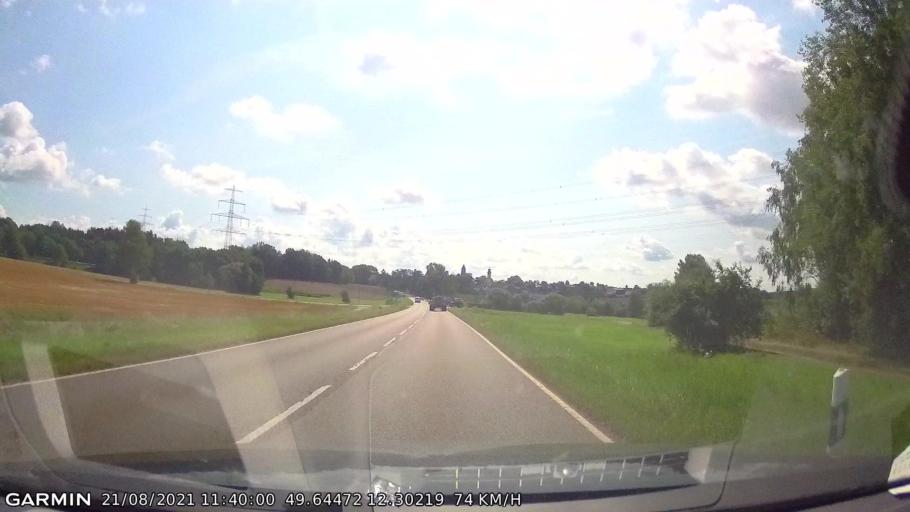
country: DE
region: Bavaria
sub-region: Upper Palatinate
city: Waldthurn
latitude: 49.6449
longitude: 12.3021
